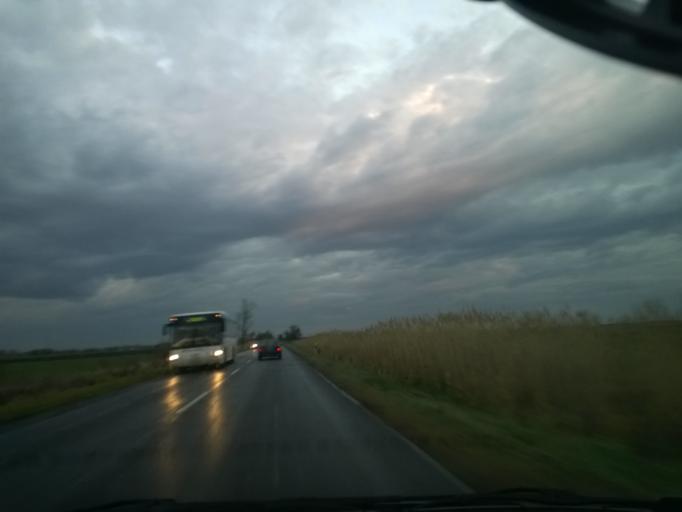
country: HU
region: Bacs-Kiskun
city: Tass
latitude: 47.0471
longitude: 19.0227
